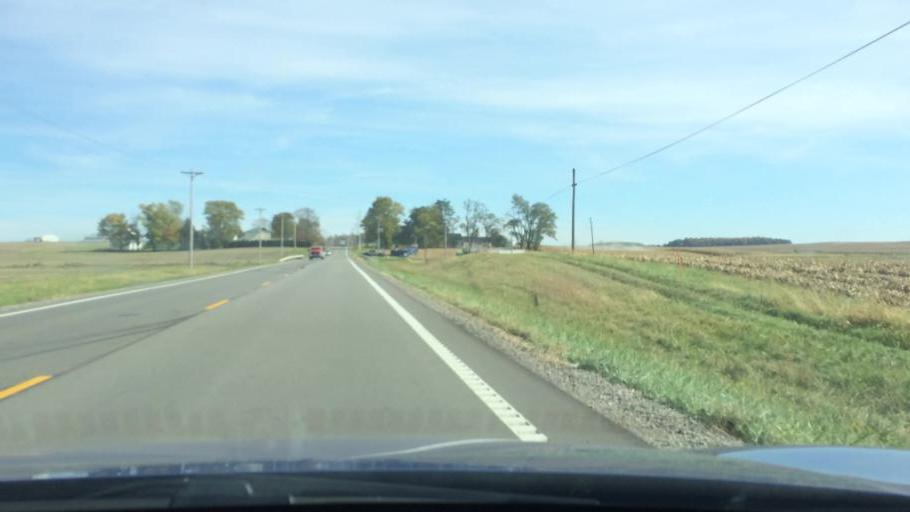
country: US
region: Ohio
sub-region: Logan County
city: Russells Point
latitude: 40.4394
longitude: -83.8866
